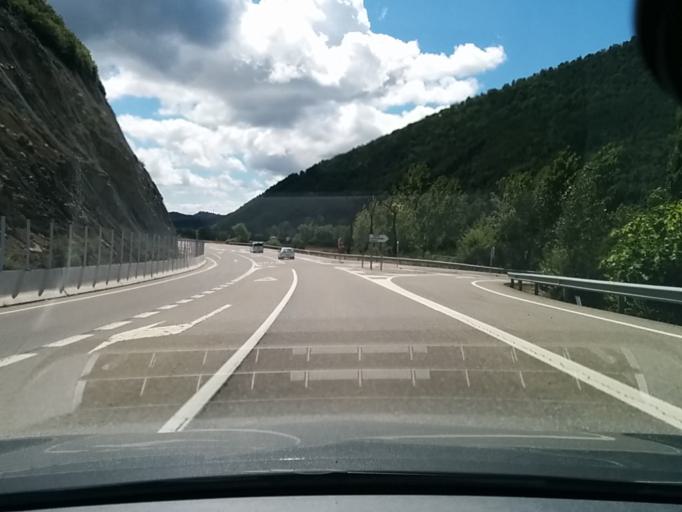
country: ES
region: Aragon
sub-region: Provincia de Huesca
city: Boltana
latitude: 42.4508
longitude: 0.0572
